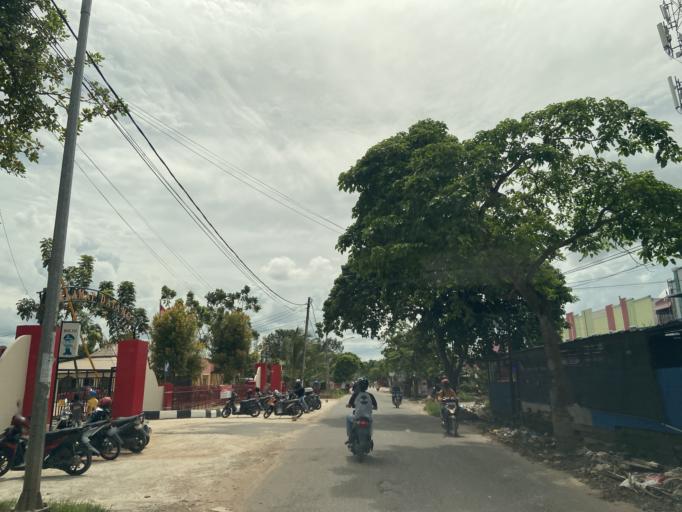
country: SG
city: Singapore
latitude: 1.0366
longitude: 103.9761
